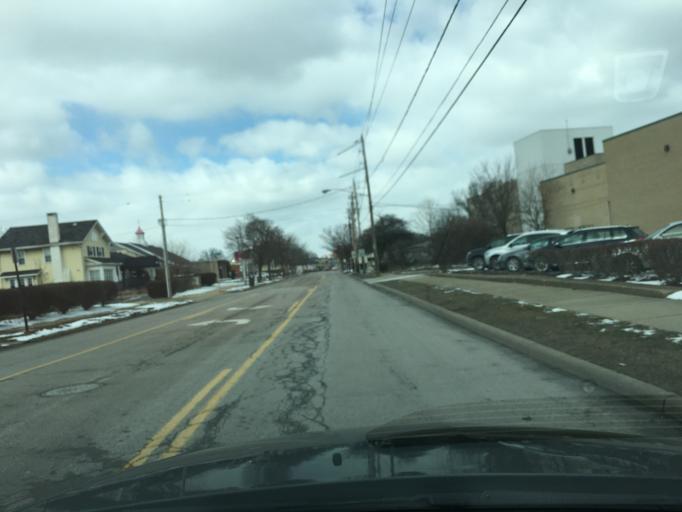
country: US
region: Ohio
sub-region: Summit County
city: Fairlawn
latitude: 41.1074
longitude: -81.5668
